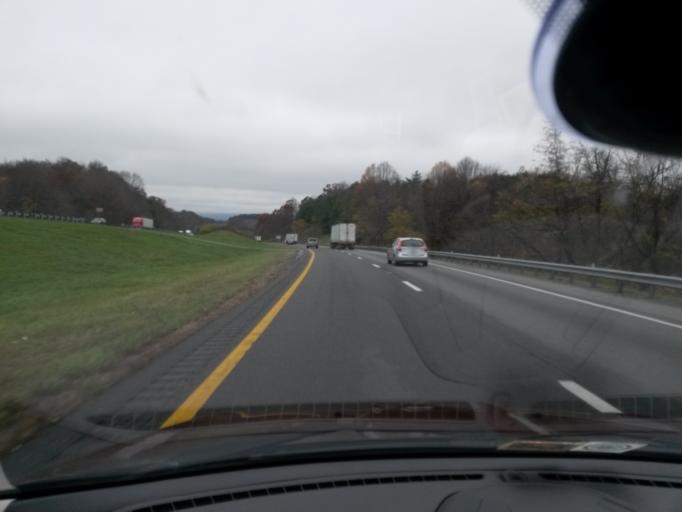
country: US
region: Virginia
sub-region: Pulaski County
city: Pulaski
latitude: 36.9038
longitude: -80.8775
